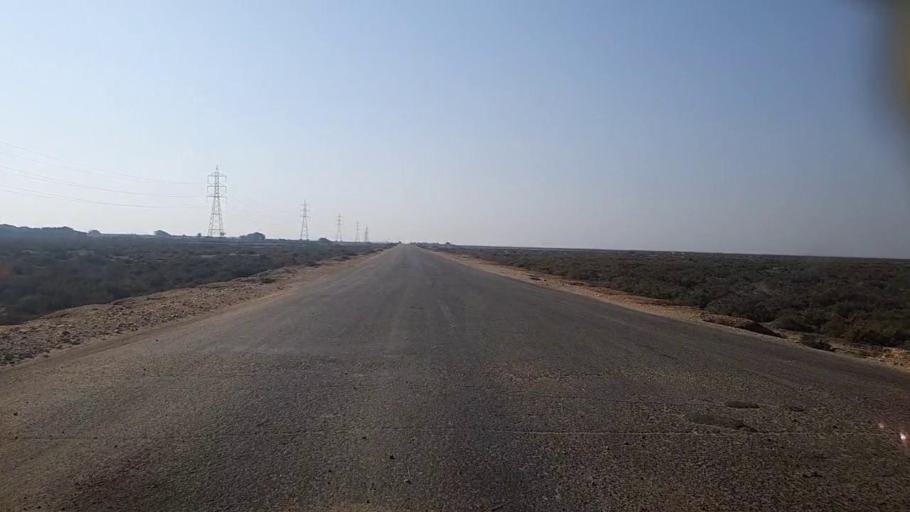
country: PK
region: Sindh
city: Gharo
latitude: 24.6248
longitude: 67.4969
